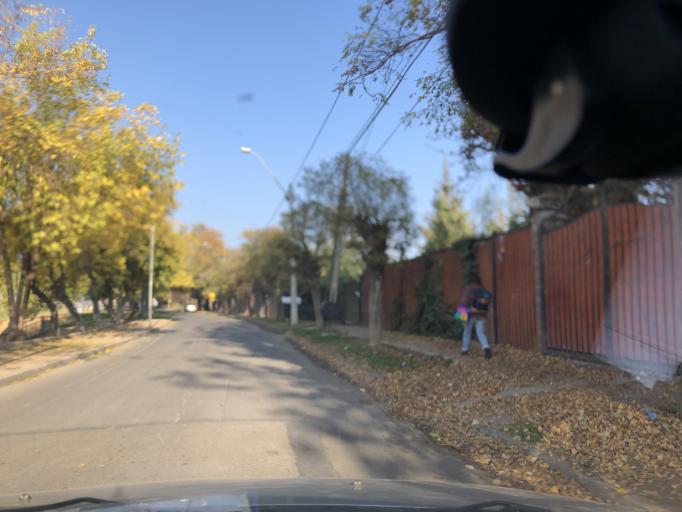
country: CL
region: Santiago Metropolitan
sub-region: Provincia de Cordillera
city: Puente Alto
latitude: -33.6248
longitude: -70.5777
